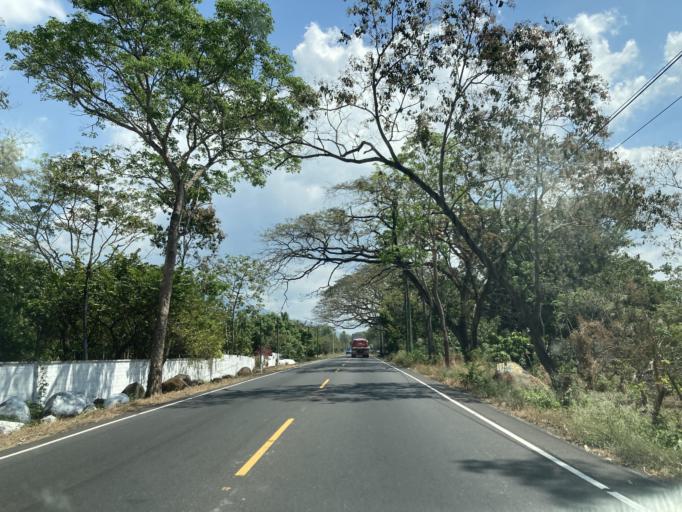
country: GT
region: Santa Rosa
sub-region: Municipio de Taxisco
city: Taxisco
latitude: 14.0925
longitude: -90.5579
